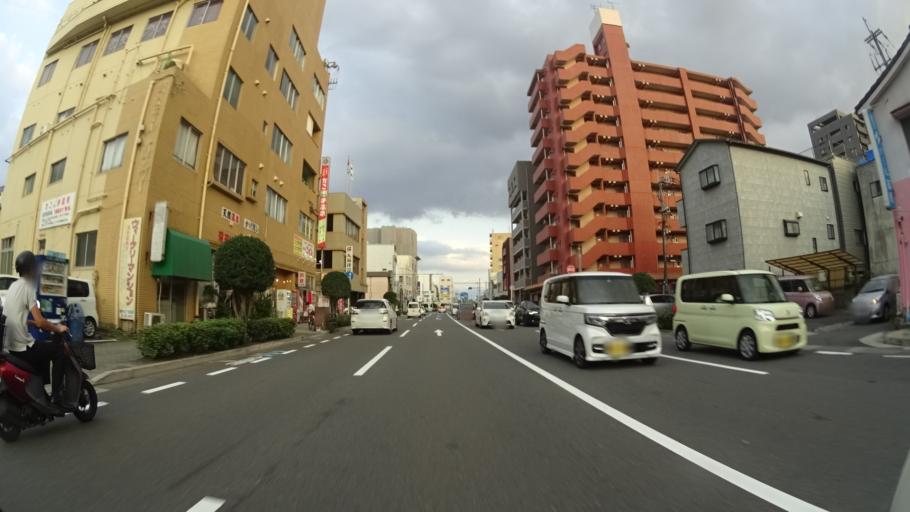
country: JP
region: Kagoshima
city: Kagoshima-shi
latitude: 31.5975
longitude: 130.5591
